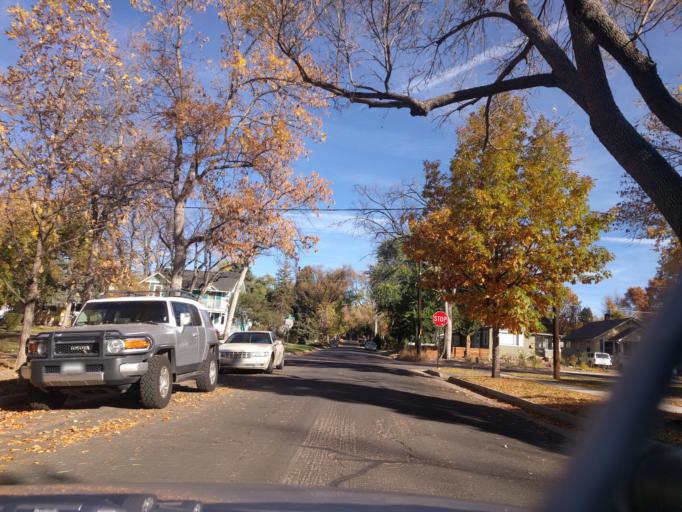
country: US
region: Colorado
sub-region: El Paso County
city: Colorado Springs
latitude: 38.8513
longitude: -104.8112
